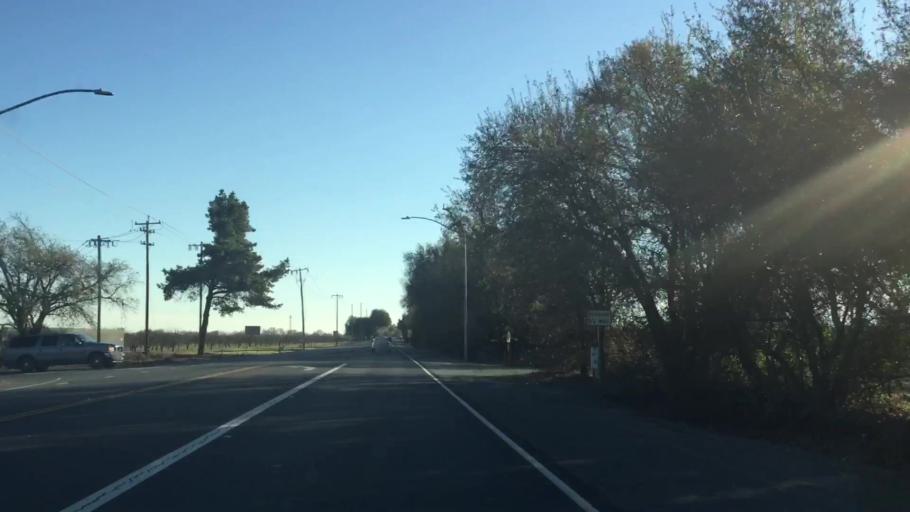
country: US
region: California
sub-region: Sutter County
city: Live Oak
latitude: 39.3213
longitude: -121.5962
